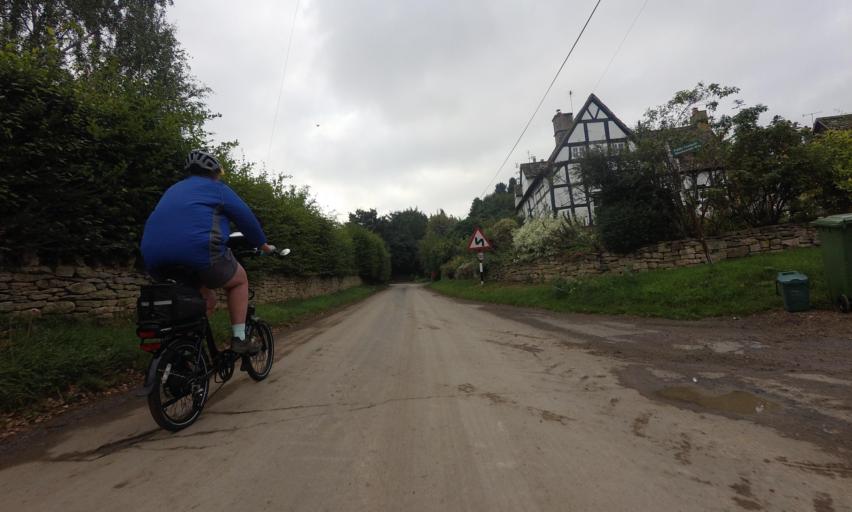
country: GB
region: England
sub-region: Gloucestershire
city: Gotherington
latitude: 51.9901
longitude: -2.0264
